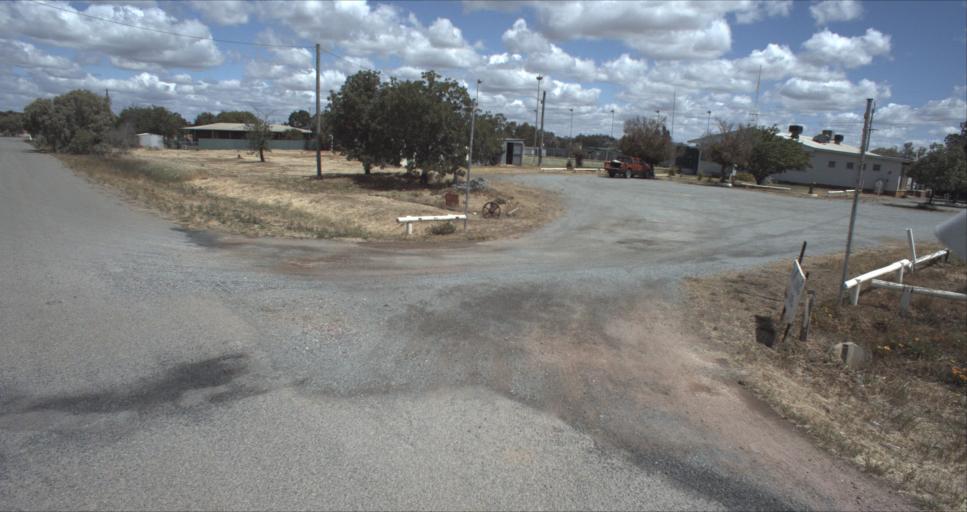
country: AU
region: New South Wales
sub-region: Murrumbidgee Shire
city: Darlington Point
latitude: -34.5159
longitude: 146.1779
